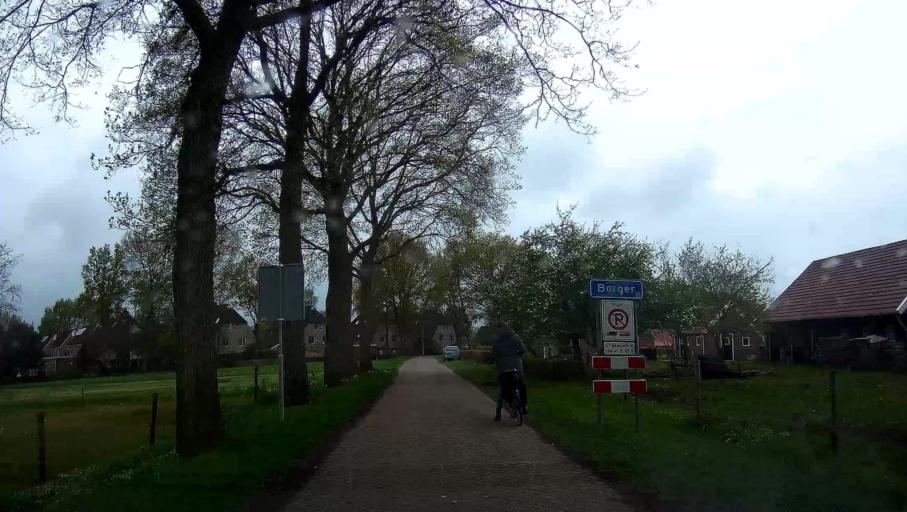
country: NL
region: Drenthe
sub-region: Gemeente Borger-Odoorn
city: Borger
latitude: 52.9288
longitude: 6.7991
